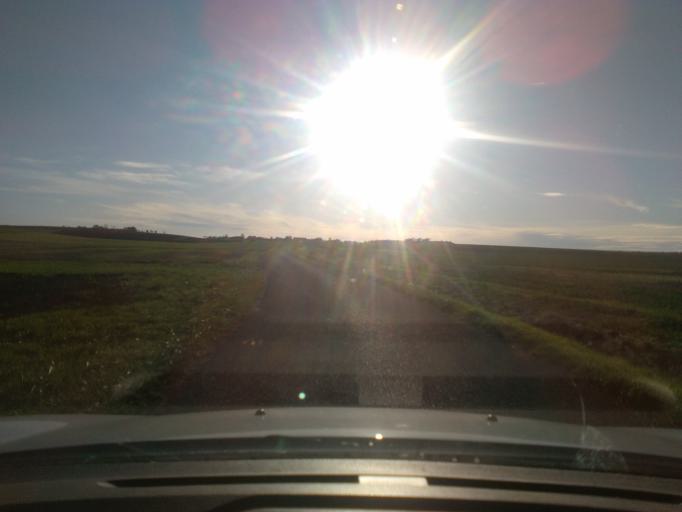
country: FR
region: Lorraine
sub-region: Departement des Vosges
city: Rambervillers
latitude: 48.2871
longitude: 6.5900
